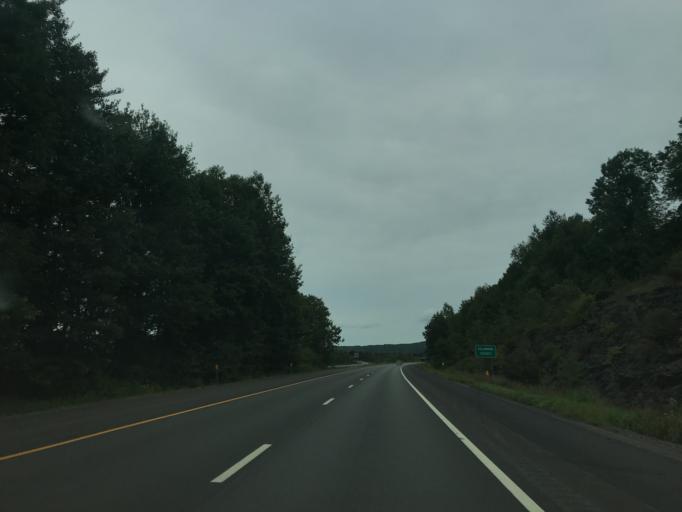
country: US
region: New York
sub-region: Delaware County
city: Sidney
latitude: 42.2928
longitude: -75.4171
